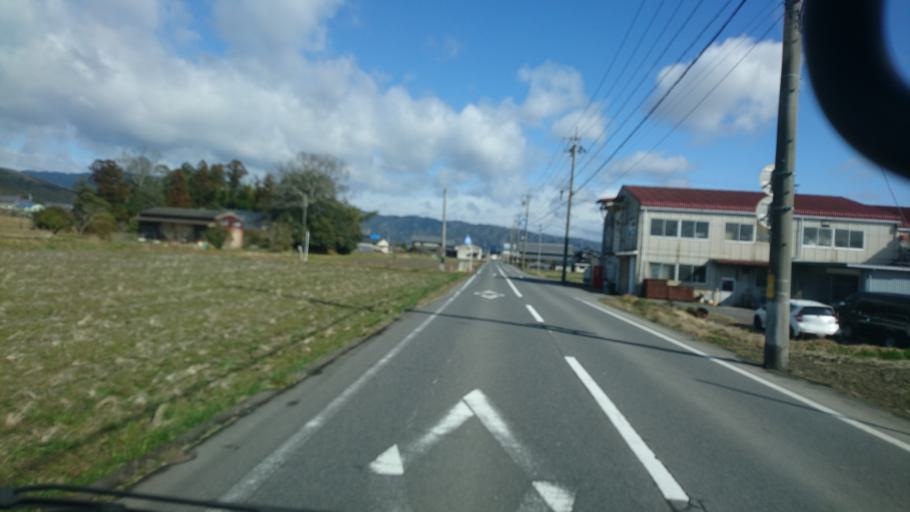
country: JP
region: Mie
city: Ueno-ebisumachi
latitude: 34.7549
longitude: 136.1112
